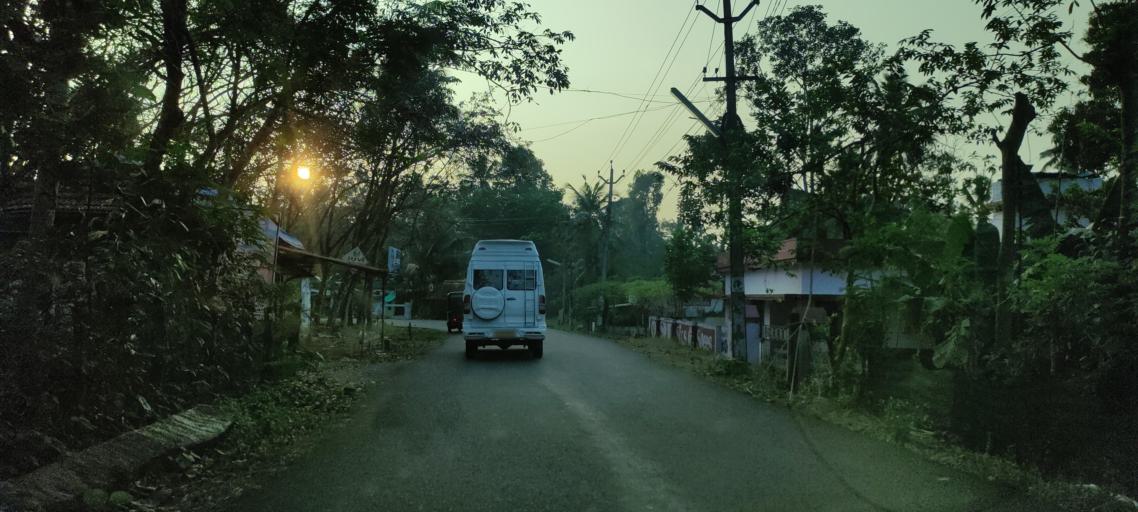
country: IN
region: Kerala
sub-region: Alappuzha
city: Kattanam
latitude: 9.1438
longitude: 76.5672
